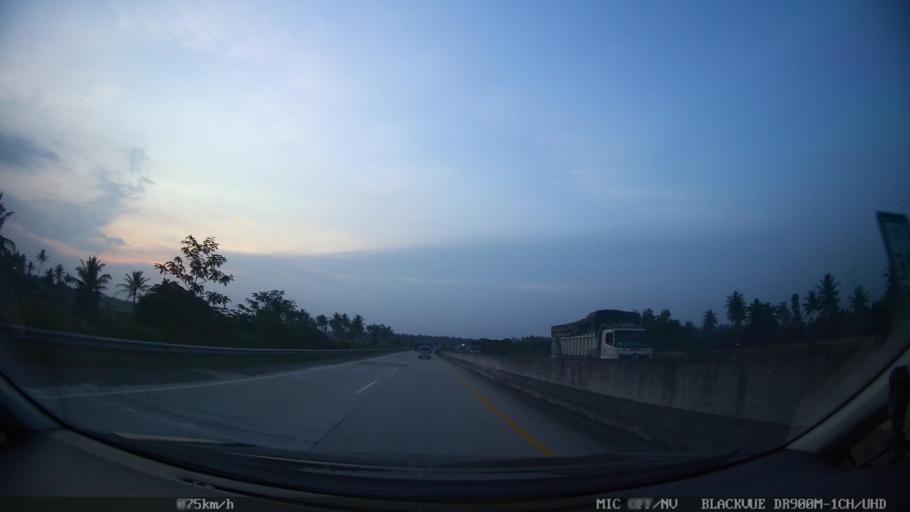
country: ID
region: Lampung
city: Kalianda
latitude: -5.6670
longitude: 105.5971
